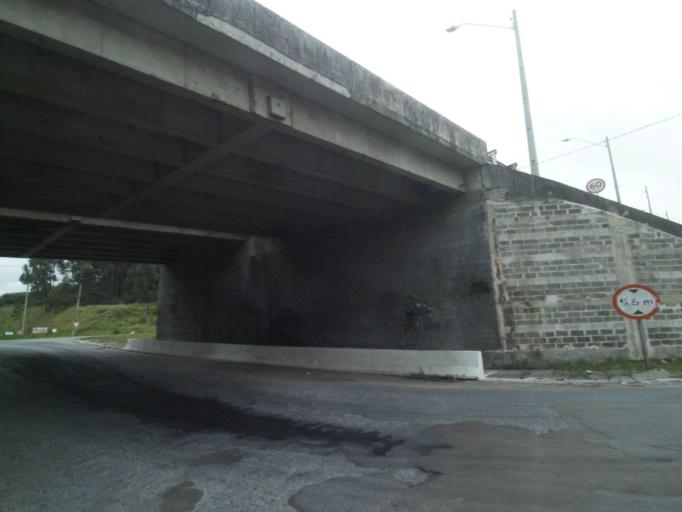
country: BR
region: Parana
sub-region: Araucaria
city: Araucaria
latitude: -25.5567
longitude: -49.3472
